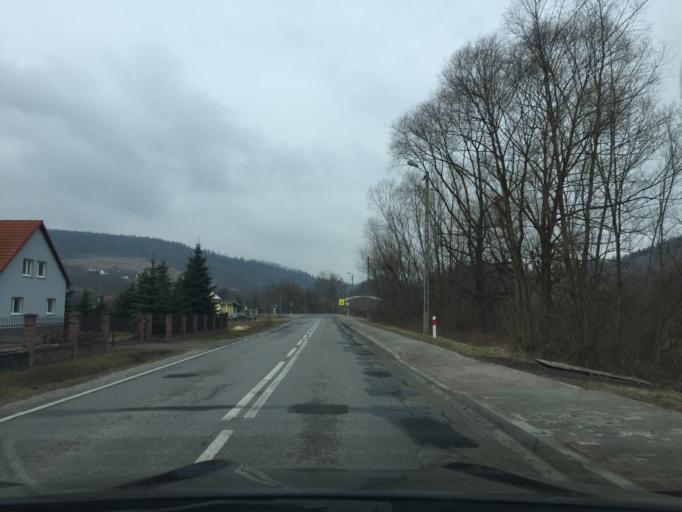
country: PL
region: Lesser Poland Voivodeship
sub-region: Powiat suski
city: Budzow
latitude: 49.7706
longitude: 19.6411
